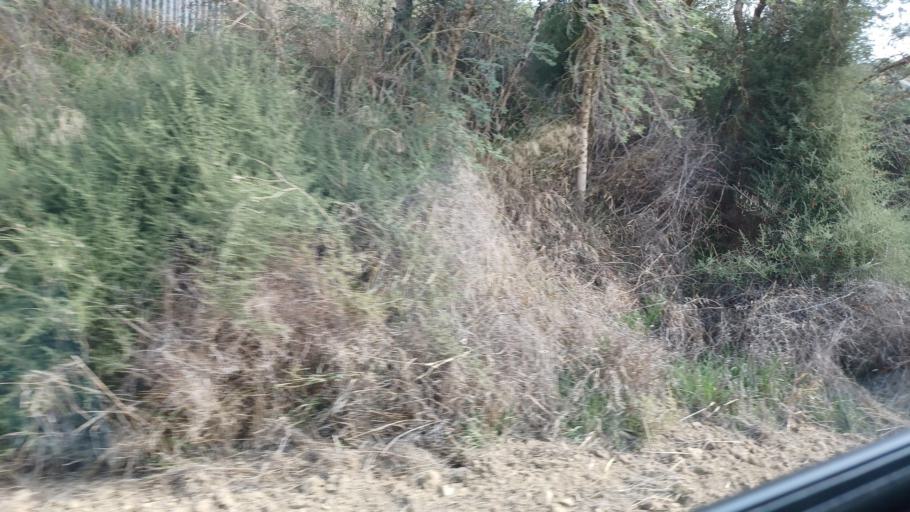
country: CY
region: Pafos
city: Polis
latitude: 34.9849
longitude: 32.4543
